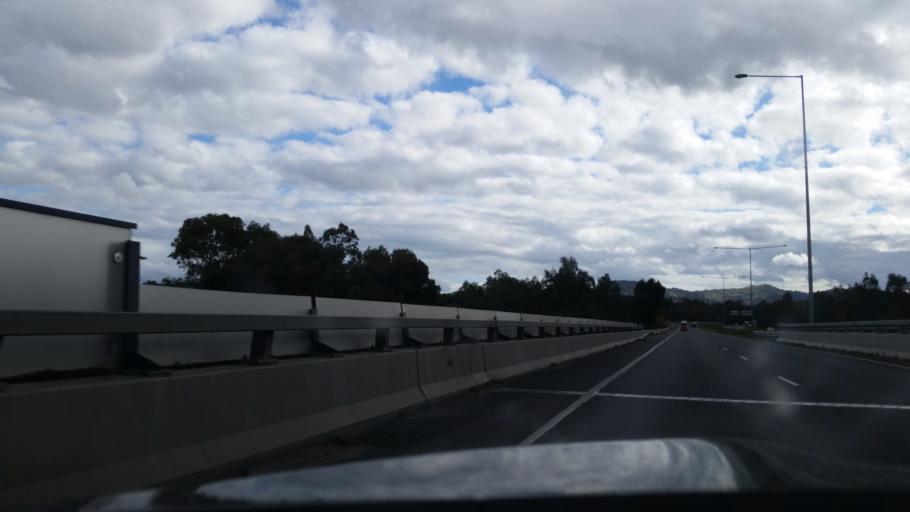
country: AU
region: Victoria
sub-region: Wodonga
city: Wodonga
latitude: -36.1107
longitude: 146.8941
